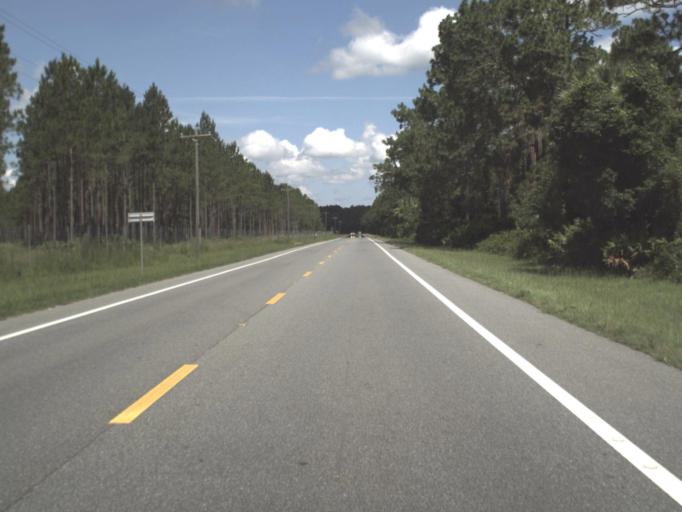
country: US
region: Florida
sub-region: Putnam County
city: Interlachen
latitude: 29.7134
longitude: -81.7976
